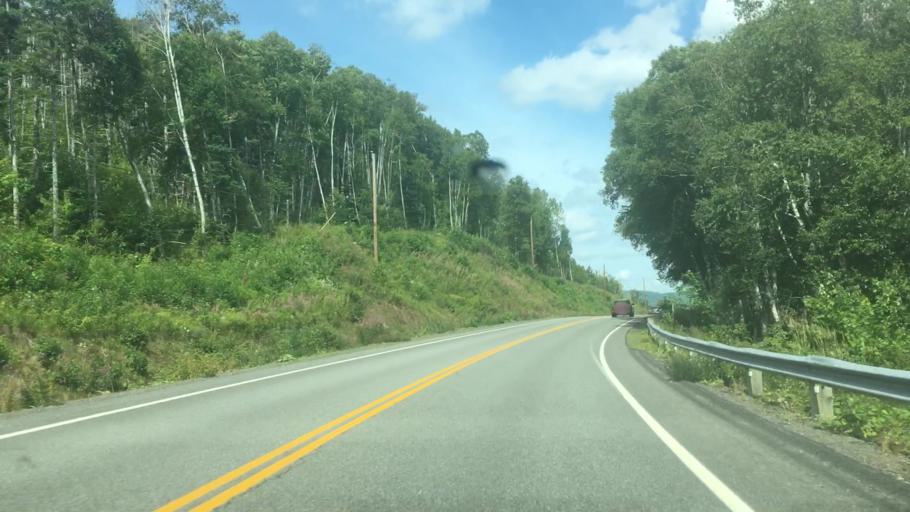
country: CA
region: Nova Scotia
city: Sydney Mines
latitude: 46.2699
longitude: -60.6093
